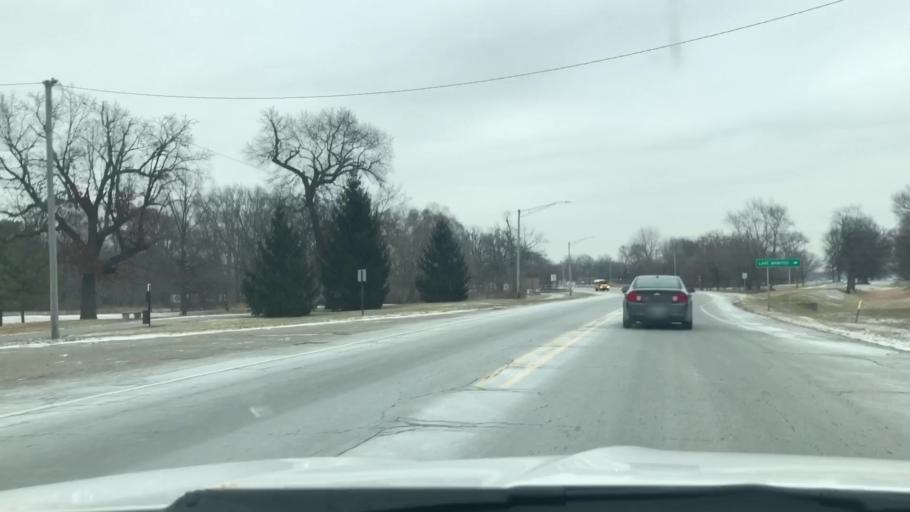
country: US
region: Indiana
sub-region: Fulton County
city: Rochester
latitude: 41.0624
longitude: -86.2000
